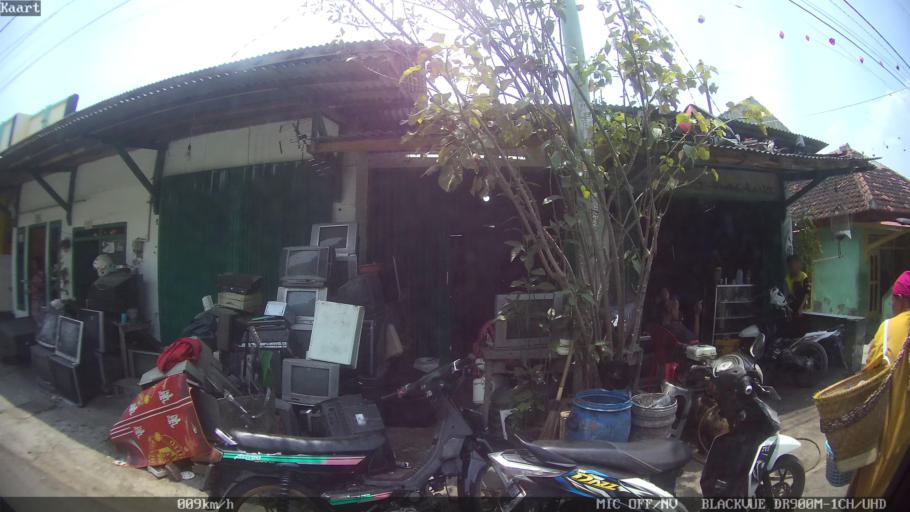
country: ID
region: Lampung
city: Bandarlampung
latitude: -5.4539
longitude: 105.2594
